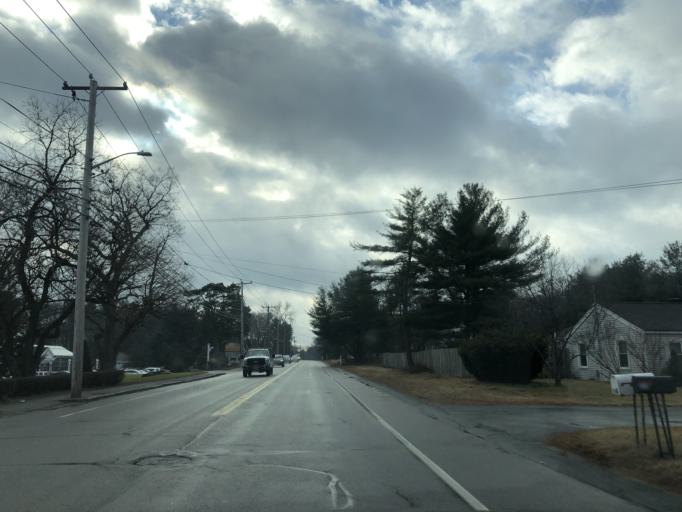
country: US
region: Massachusetts
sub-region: Norfolk County
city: Plainville
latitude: 41.9928
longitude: -71.2908
